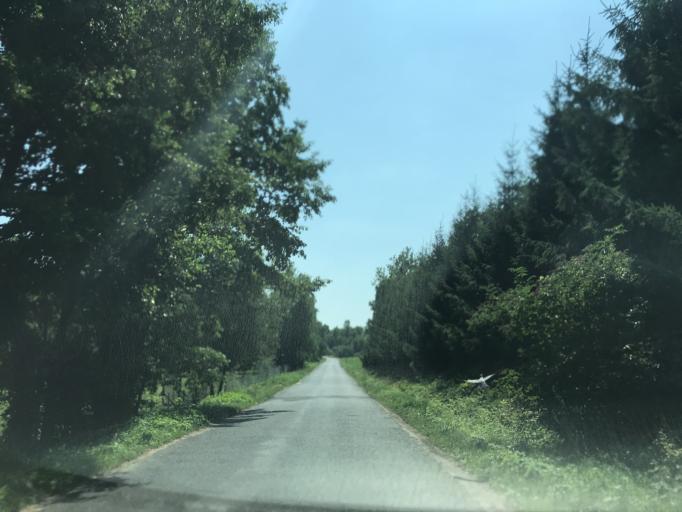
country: PL
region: Kujawsko-Pomorskie
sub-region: Powiat golubsko-dobrzynski
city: Zbojno
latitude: 52.9940
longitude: 19.2116
